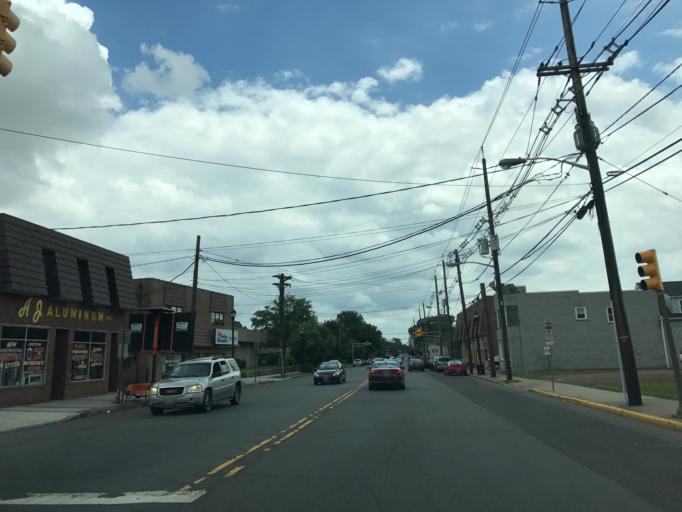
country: US
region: New Jersey
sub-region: Union County
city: Linden
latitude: 40.6290
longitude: -74.2488
